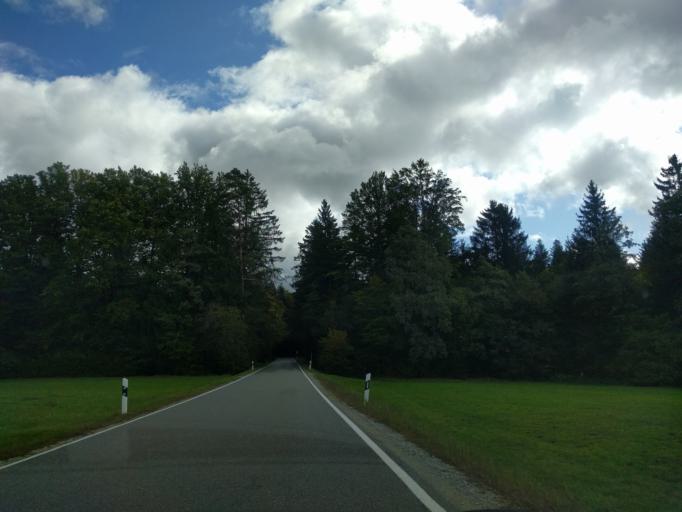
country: DE
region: Bavaria
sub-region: Lower Bavaria
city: Schaufling
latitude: 48.8333
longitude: 13.0525
